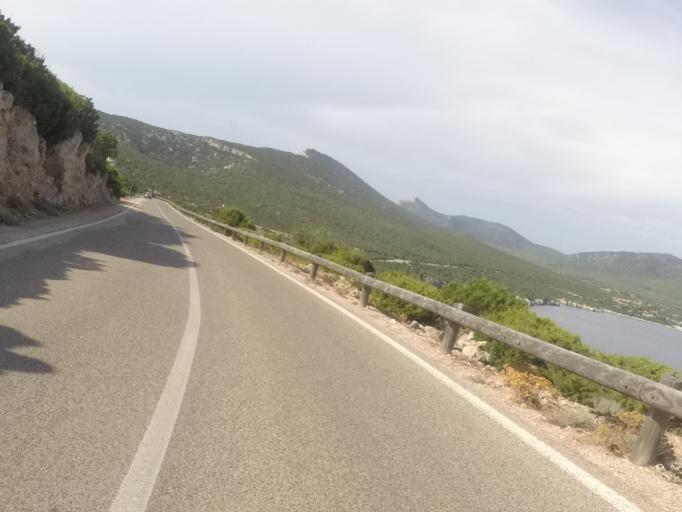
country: IT
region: Sardinia
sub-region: Provincia di Sassari
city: Alghero
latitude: 40.5719
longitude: 8.1630
